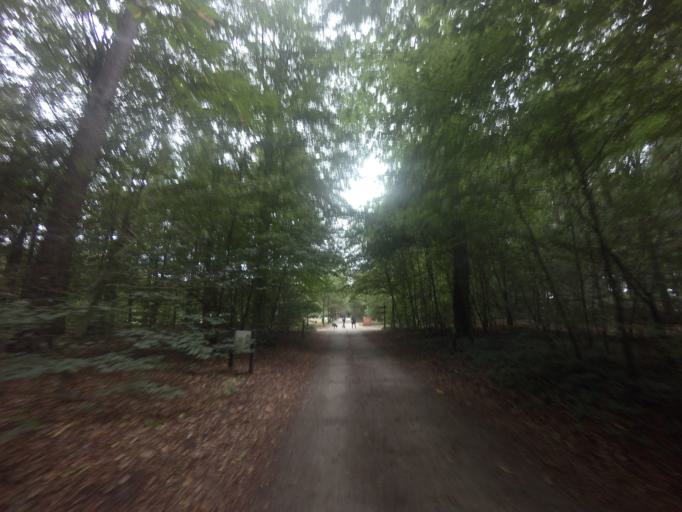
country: NL
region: Drenthe
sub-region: Gemeente Westerveld
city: Dwingeloo
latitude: 52.9501
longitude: 6.3113
